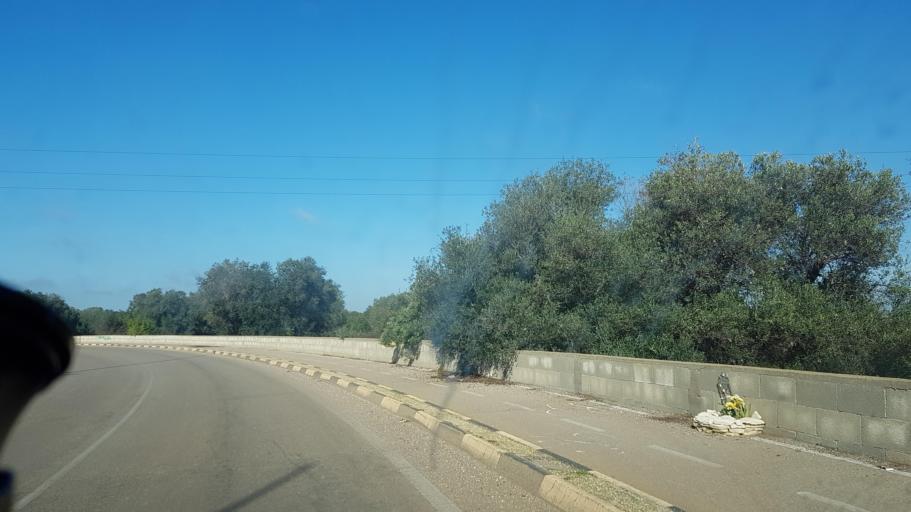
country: IT
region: Apulia
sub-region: Provincia di Brindisi
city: San Vito dei Normanni
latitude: 40.6639
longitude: 17.7142
